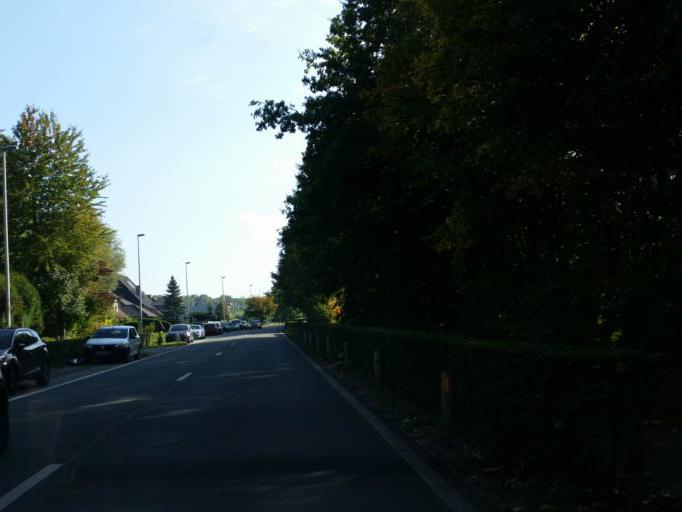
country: BE
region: Flanders
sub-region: Provincie Antwerpen
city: Edegem
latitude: 51.1576
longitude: 4.4146
